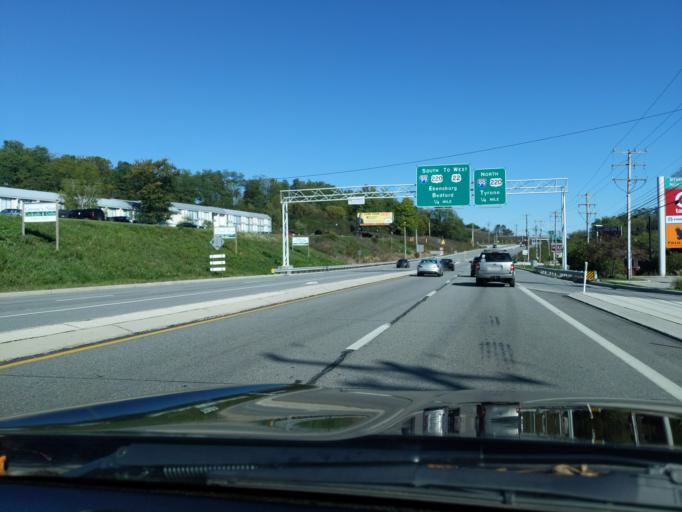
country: US
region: Pennsylvania
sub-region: Blair County
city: Lakemont
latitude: 40.4598
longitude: -78.4092
